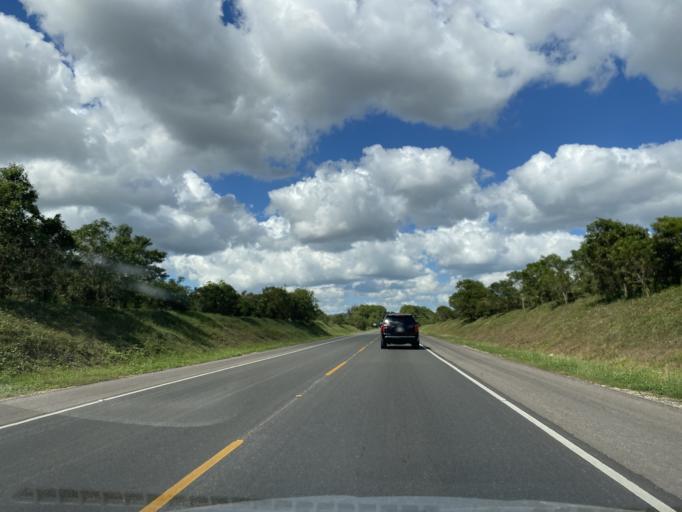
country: DO
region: Monte Plata
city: Monte Plata
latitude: 18.7440
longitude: -69.7647
